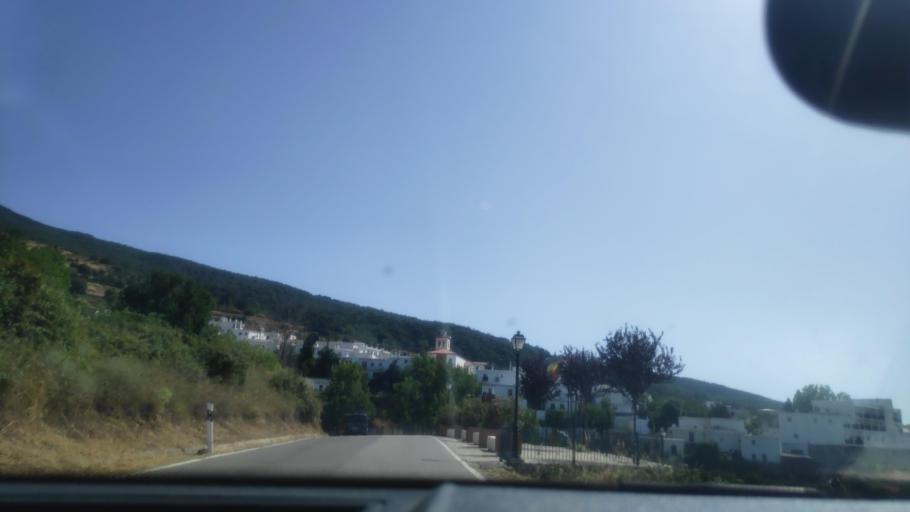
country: ES
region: Andalusia
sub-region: Provincia de Granada
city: Portugos
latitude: 36.9402
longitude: -3.3133
